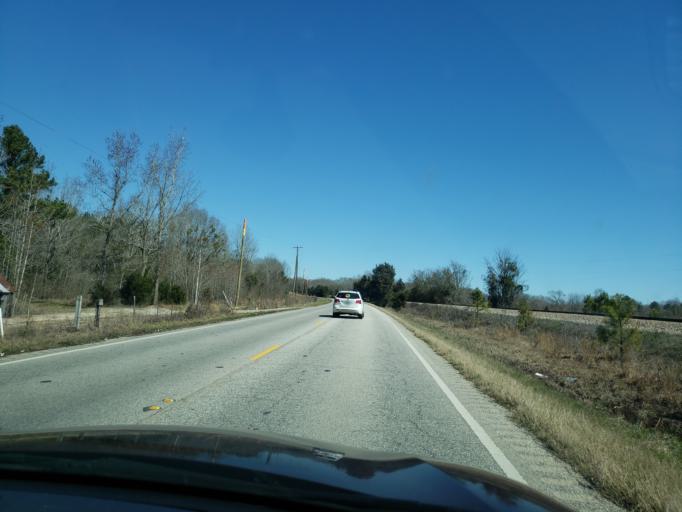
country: US
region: Alabama
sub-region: Lee County
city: Auburn
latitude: 32.5960
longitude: -85.6168
